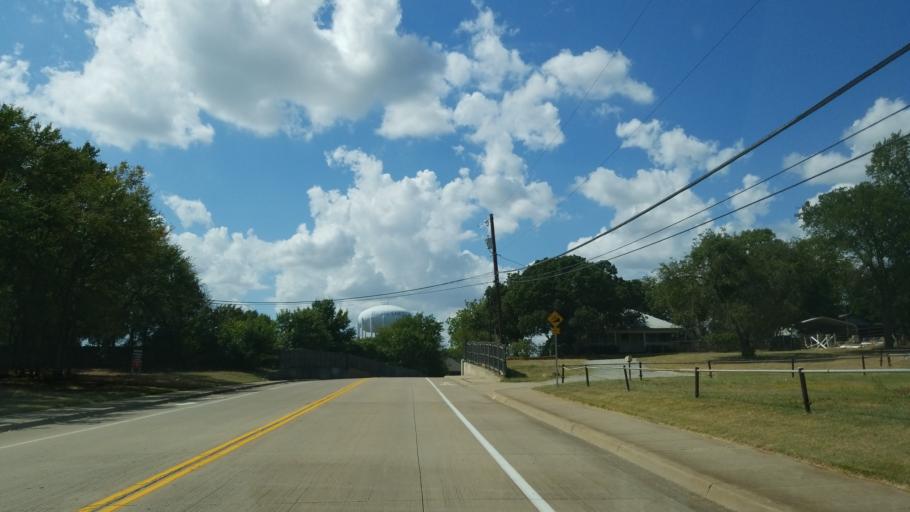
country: US
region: Texas
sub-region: Tarrant County
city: Euless
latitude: 32.8592
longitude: -97.1078
